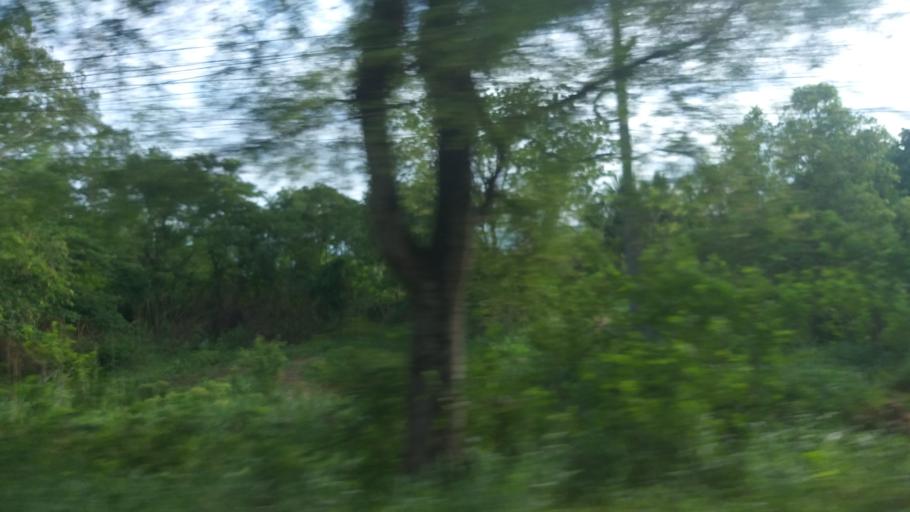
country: TH
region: Chaiyaphum
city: Ban Thaen
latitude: 16.3826
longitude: 102.3083
